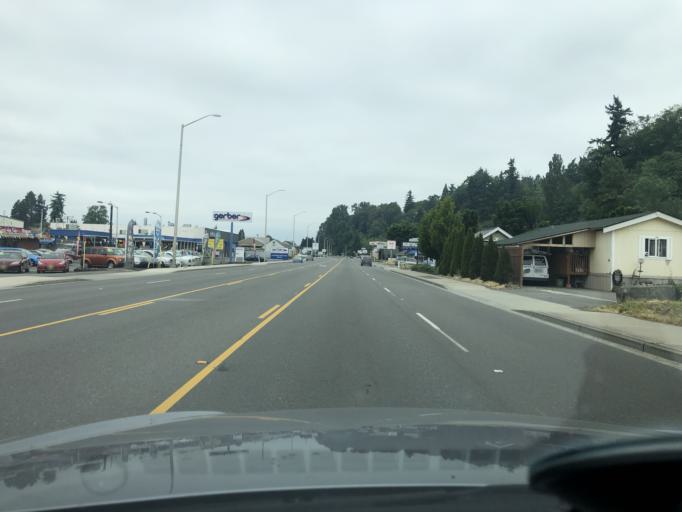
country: US
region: Washington
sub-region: King County
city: Kent
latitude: 47.3726
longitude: -122.2303
